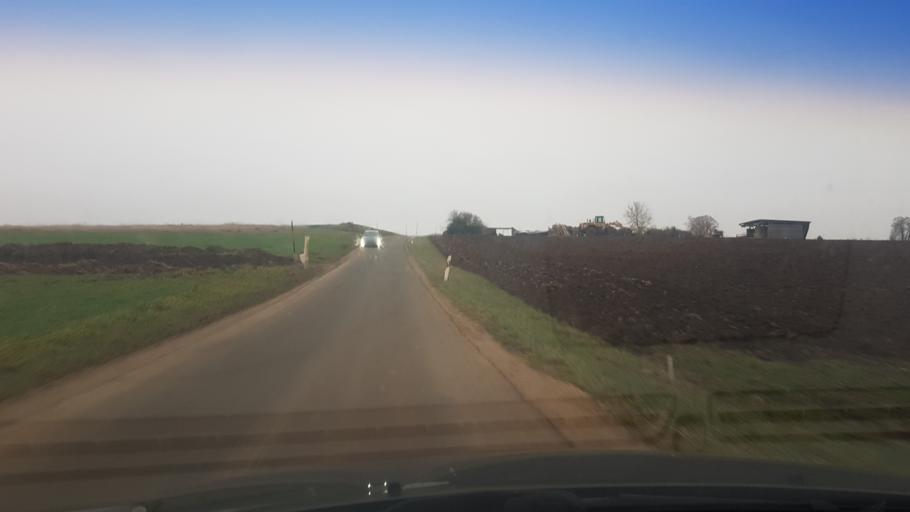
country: DE
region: Bavaria
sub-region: Upper Franconia
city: Kasendorf
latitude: 50.0395
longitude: 11.2908
